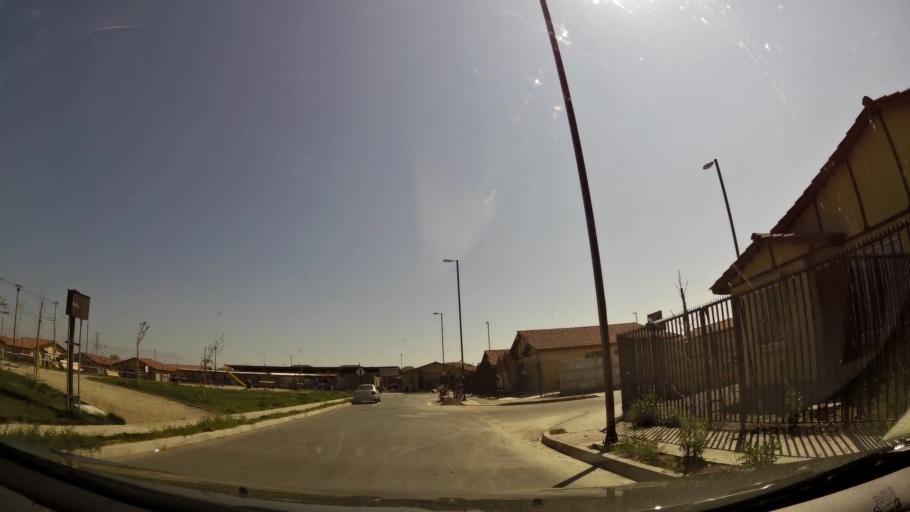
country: CL
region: Santiago Metropolitan
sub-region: Provincia de Chacabuco
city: Chicureo Abajo
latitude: -33.3286
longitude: -70.7507
